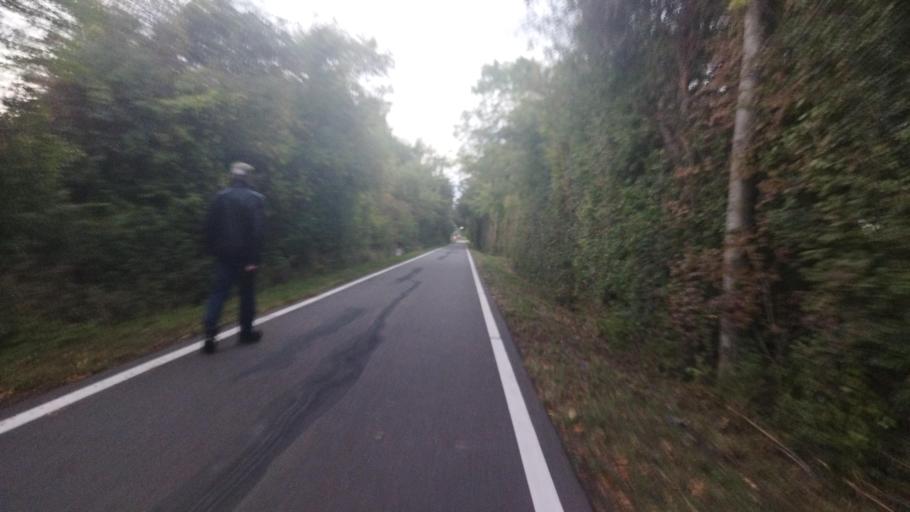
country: DE
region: North Rhine-Westphalia
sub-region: Regierungsbezirk Munster
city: Horstmar
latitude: 52.0759
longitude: 7.3209
